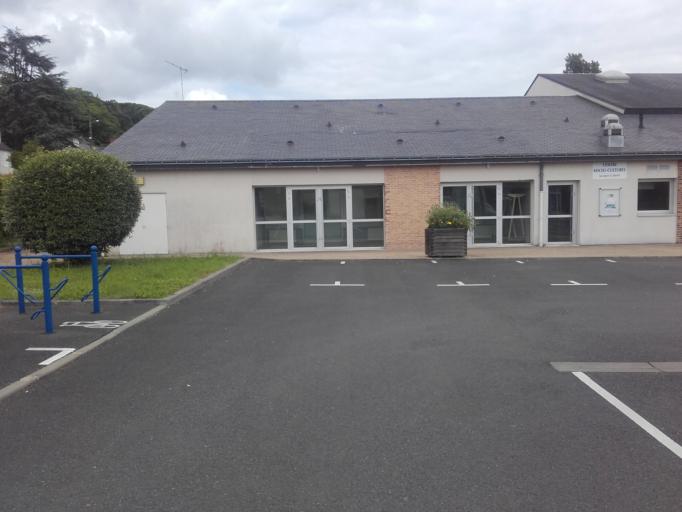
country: FR
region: Centre
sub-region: Departement d'Indre-et-Loire
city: Saint-Paterne-Racan
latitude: 47.6040
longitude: 0.4802
